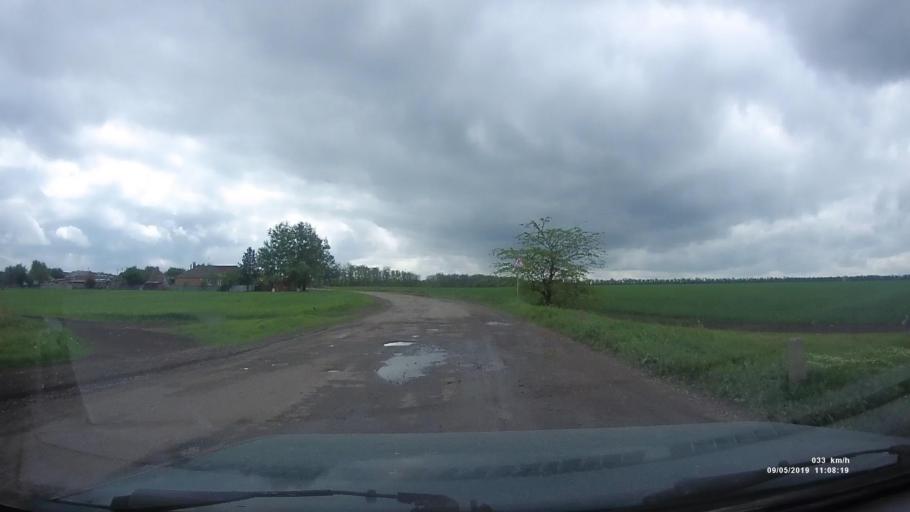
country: RU
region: Krasnodarskiy
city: Kanelovskaya
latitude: 46.7900
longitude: 39.2094
